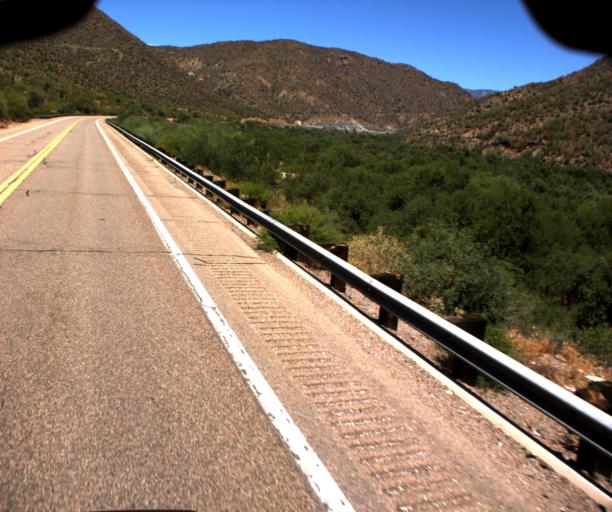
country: US
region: Arizona
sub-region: Pinal County
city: Kearny
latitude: 33.0587
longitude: -110.7210
